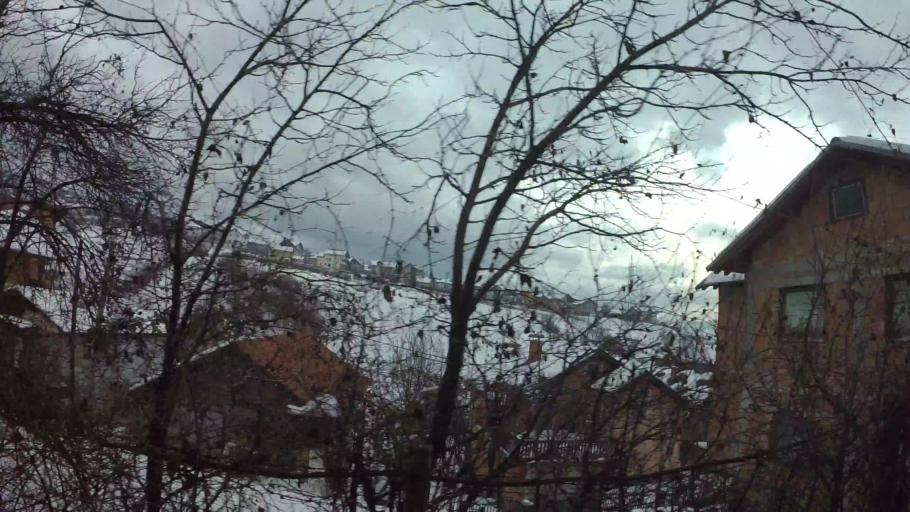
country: BA
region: Federation of Bosnia and Herzegovina
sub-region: Kanton Sarajevo
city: Sarajevo
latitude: 43.8586
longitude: 18.3273
